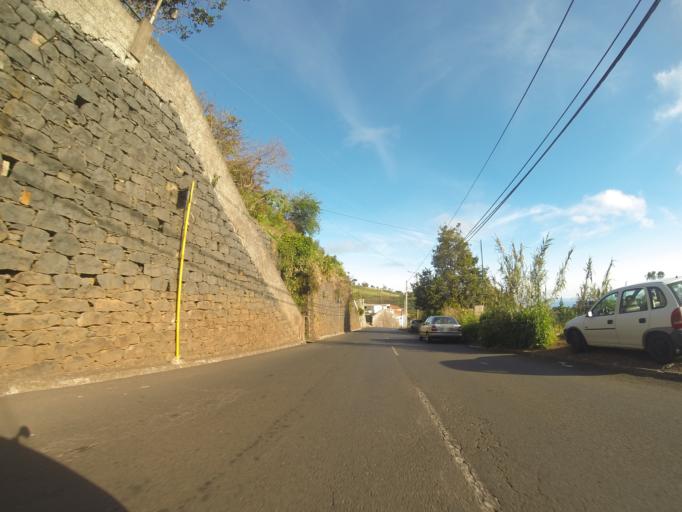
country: PT
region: Madeira
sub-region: Funchal
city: Nossa Senhora do Monte
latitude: 32.6629
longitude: -16.8720
